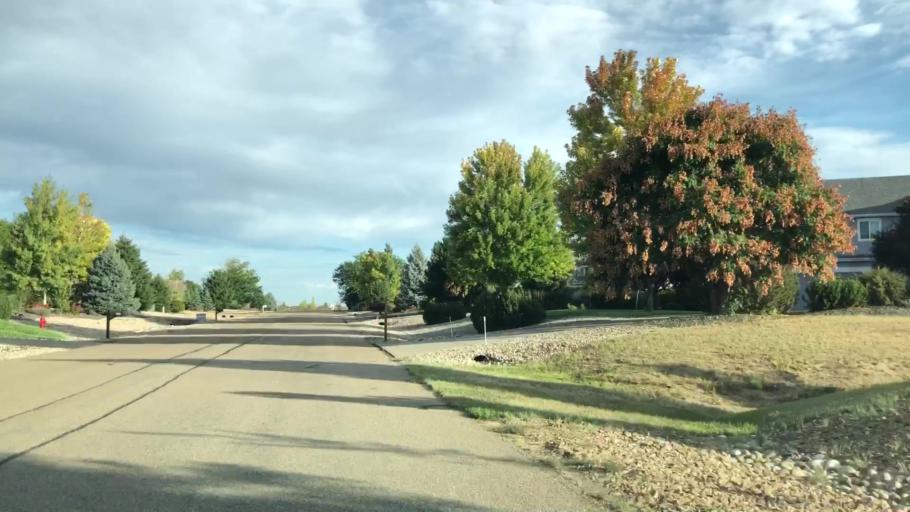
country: US
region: Colorado
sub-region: Weld County
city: Windsor
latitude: 40.4418
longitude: -104.9523
